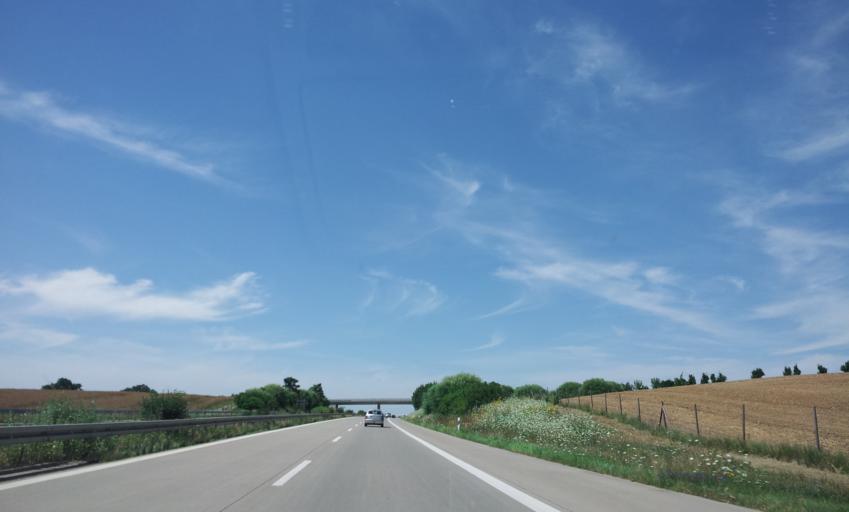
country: DE
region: Mecklenburg-Vorpommern
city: Strasburg
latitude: 53.5473
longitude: 13.6896
